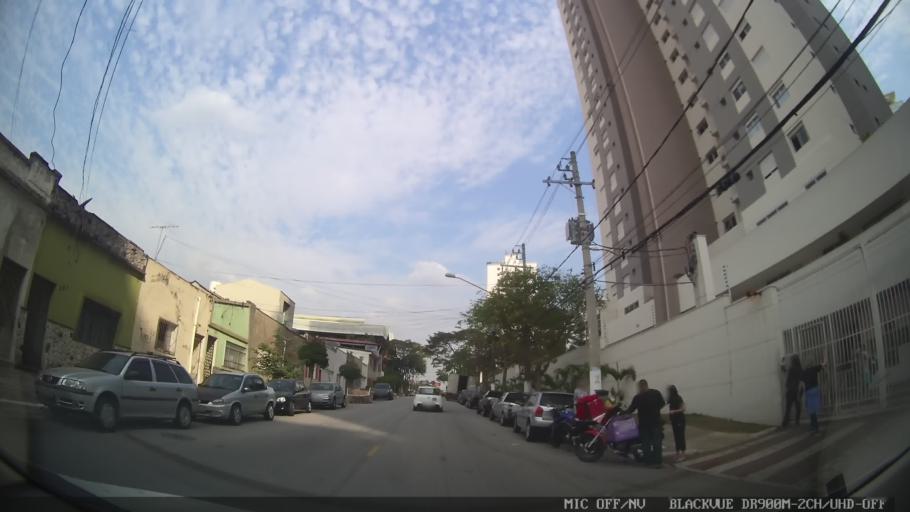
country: BR
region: Sao Paulo
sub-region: Sao Paulo
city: Sao Paulo
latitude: -23.5758
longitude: -46.6031
